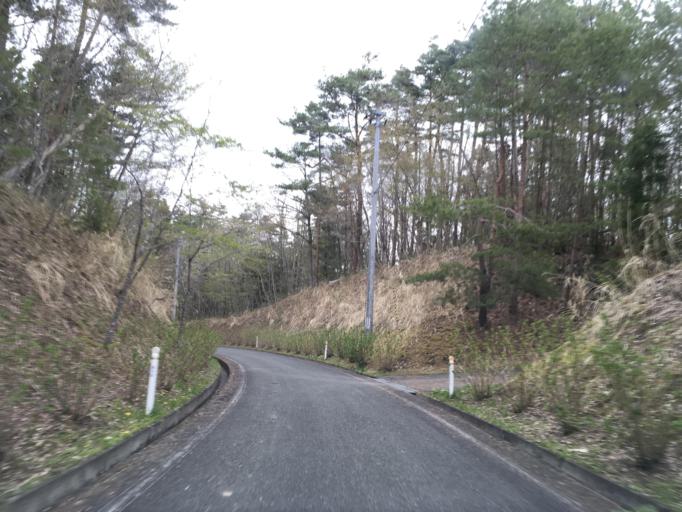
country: JP
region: Iwate
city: Ichinoseki
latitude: 38.8541
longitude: 141.3289
